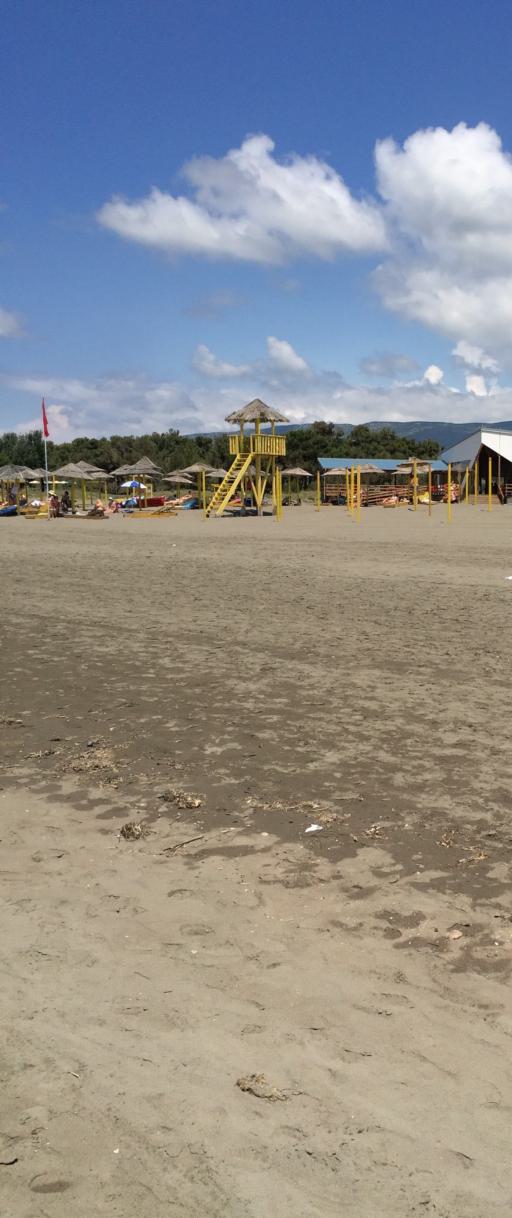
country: ME
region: Ulcinj
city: Ulcinj
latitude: 41.9079
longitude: 19.2448
